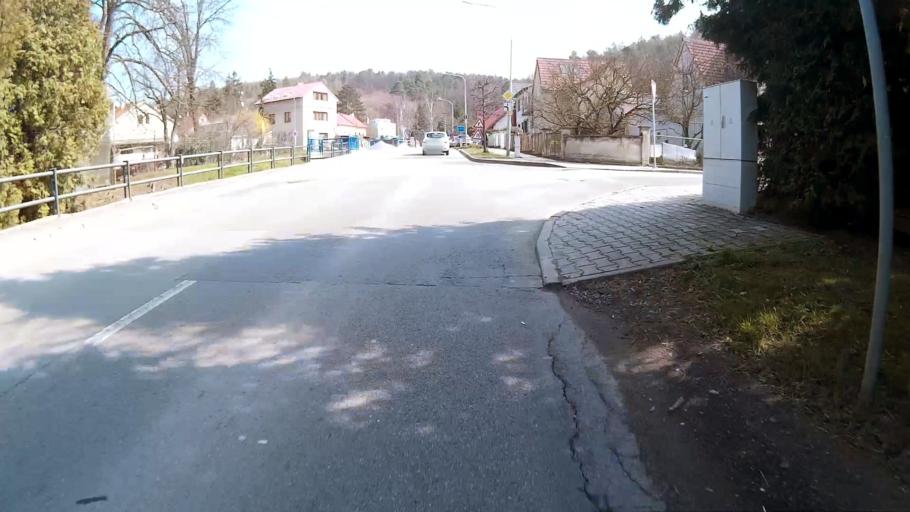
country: CZ
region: South Moravian
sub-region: Mesto Brno
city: Mokra Hora
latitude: 49.2570
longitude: 16.5928
